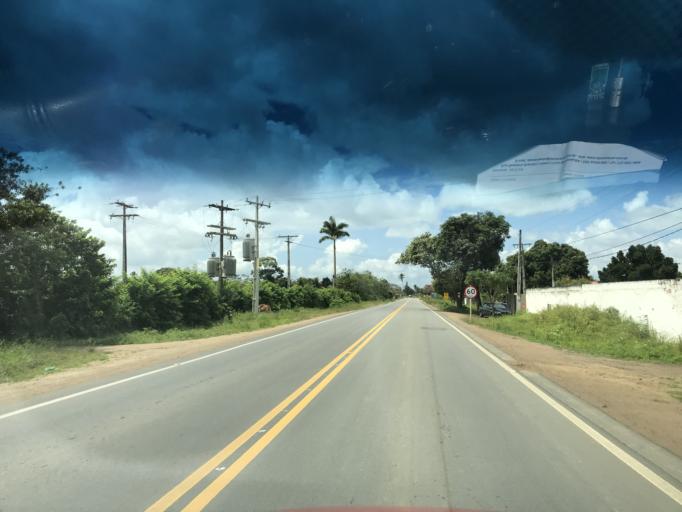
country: BR
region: Bahia
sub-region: Conceicao Do Almeida
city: Conceicao do Almeida
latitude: -12.7290
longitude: -39.1992
